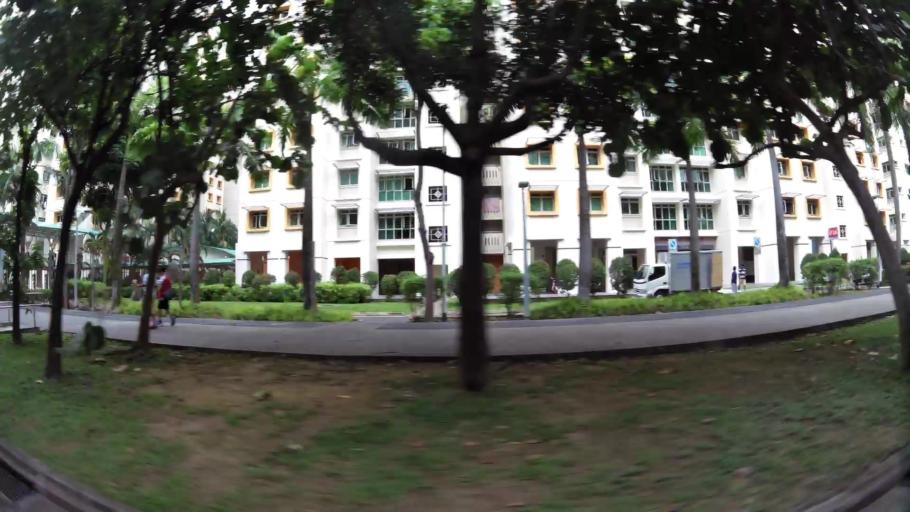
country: MY
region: Johor
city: Kampung Pasir Gudang Baru
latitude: 1.3969
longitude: 103.9092
